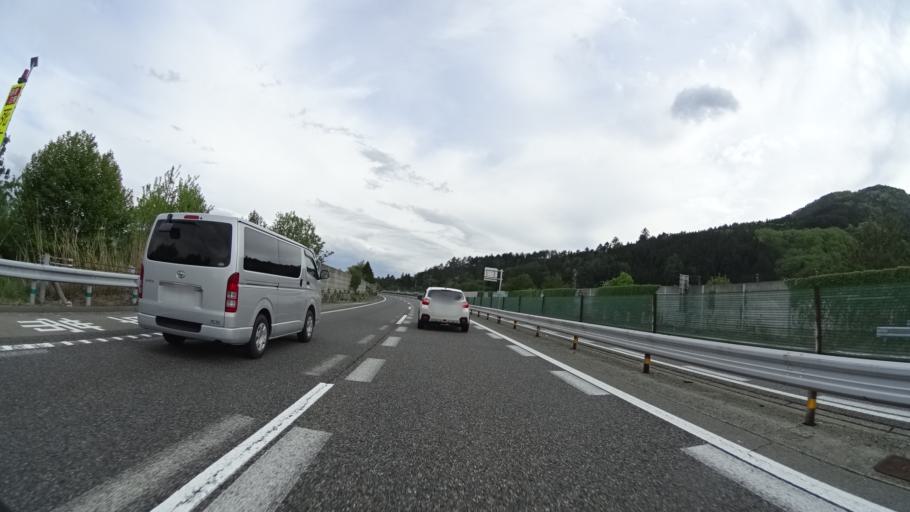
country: JP
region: Nagano
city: Ina
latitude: 35.8329
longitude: 137.9280
